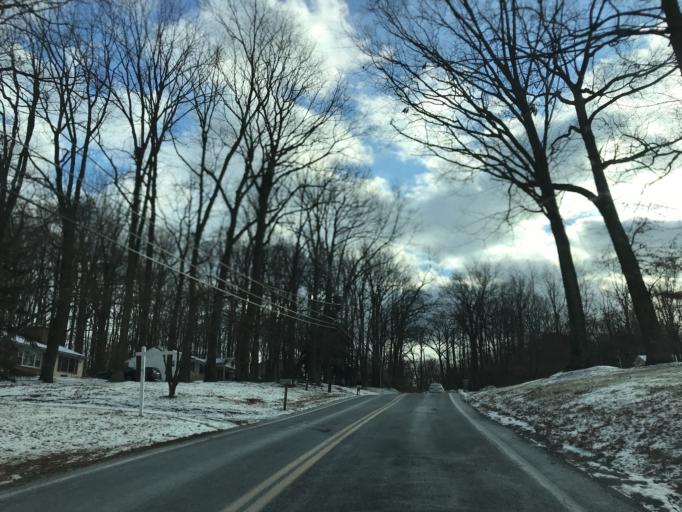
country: US
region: Maryland
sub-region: Harford County
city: Bel Air North
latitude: 39.6497
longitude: -76.3820
